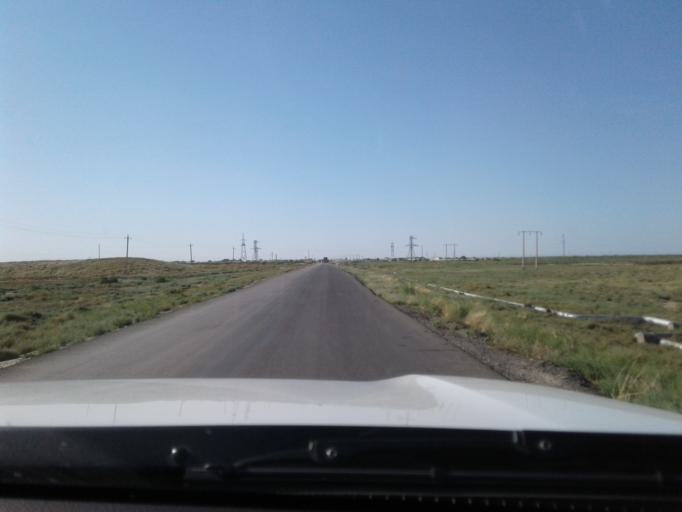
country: IR
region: Razavi Khorasan
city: Kalat-e Naderi
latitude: 37.1809
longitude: 60.0421
